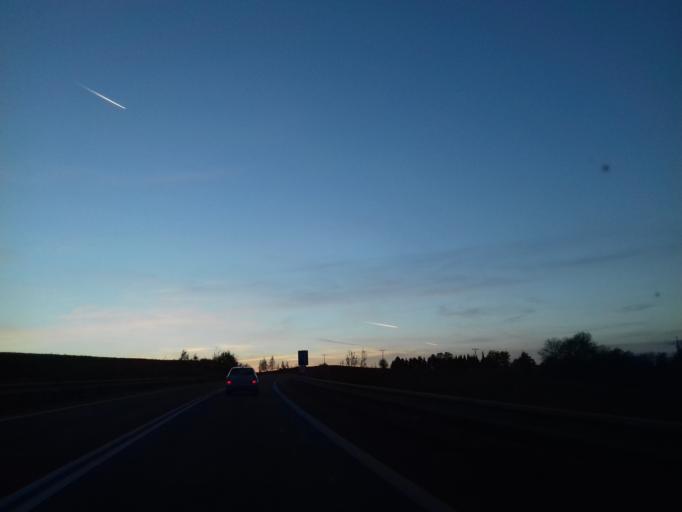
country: CZ
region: Vysocina
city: Pribyslav
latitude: 49.6384
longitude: 15.6974
